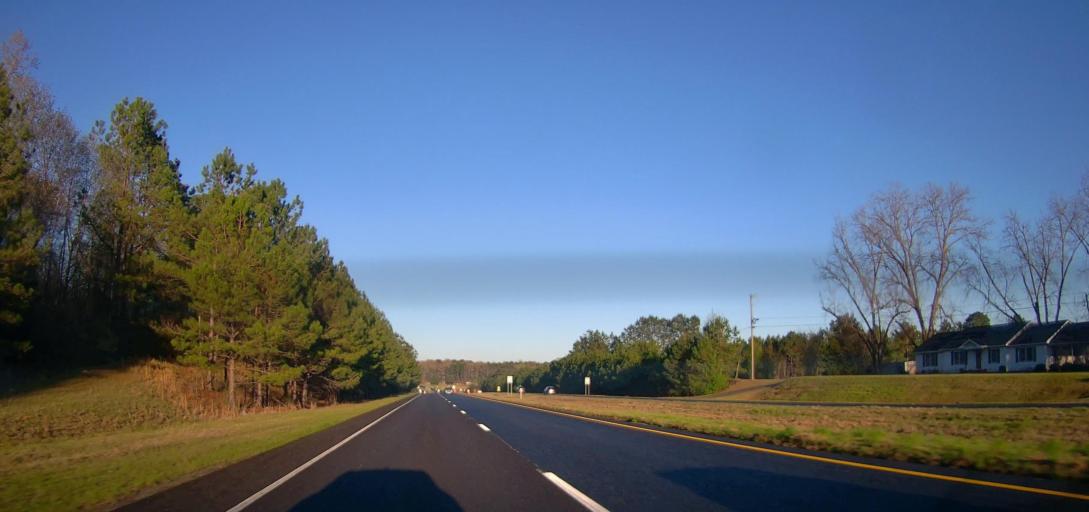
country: US
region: Georgia
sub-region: Wilkinson County
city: Gordon
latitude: 32.8482
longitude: -83.4286
